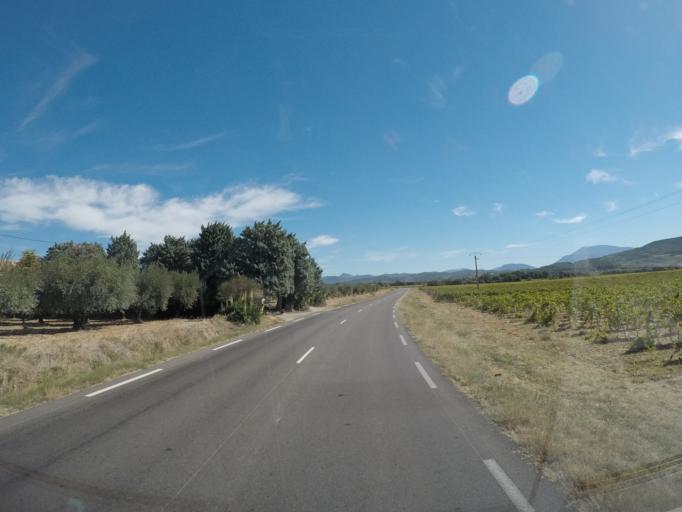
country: FR
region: Provence-Alpes-Cote d'Azur
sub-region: Departement du Vaucluse
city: Visan
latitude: 44.2909
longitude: 4.9656
